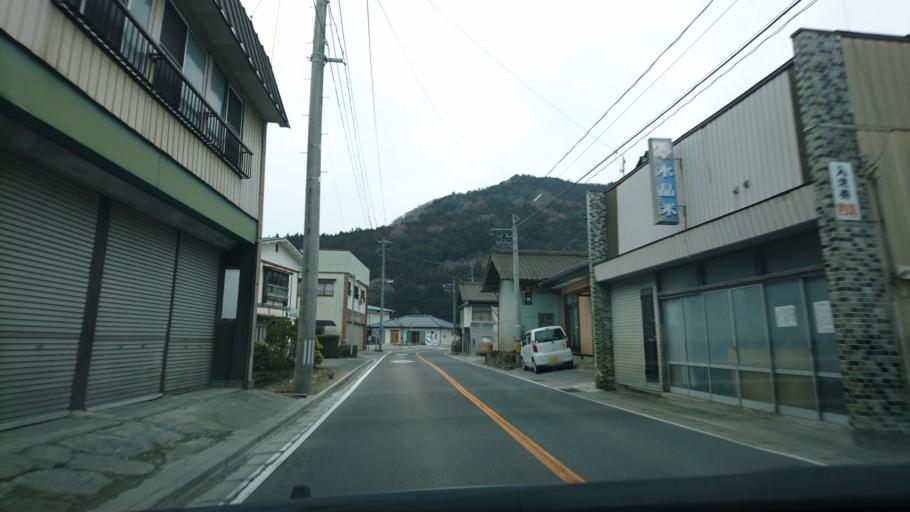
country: JP
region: Iwate
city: Tono
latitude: 39.1512
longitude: 141.5408
